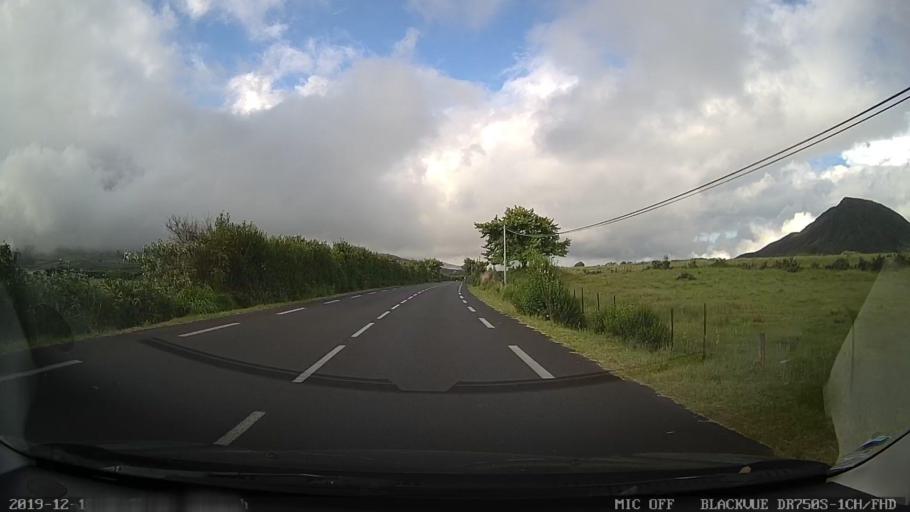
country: RE
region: Reunion
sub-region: Reunion
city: Le Tampon
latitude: -21.1824
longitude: 55.5794
